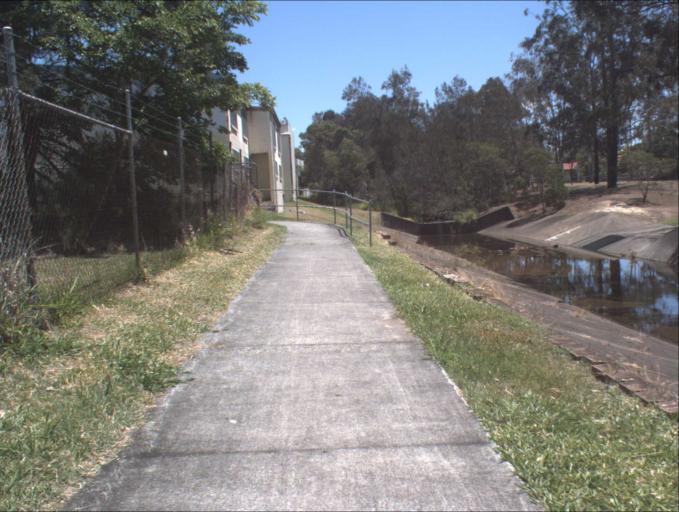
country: AU
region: Queensland
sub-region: Logan
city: Rochedale South
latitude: -27.6060
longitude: 153.1142
